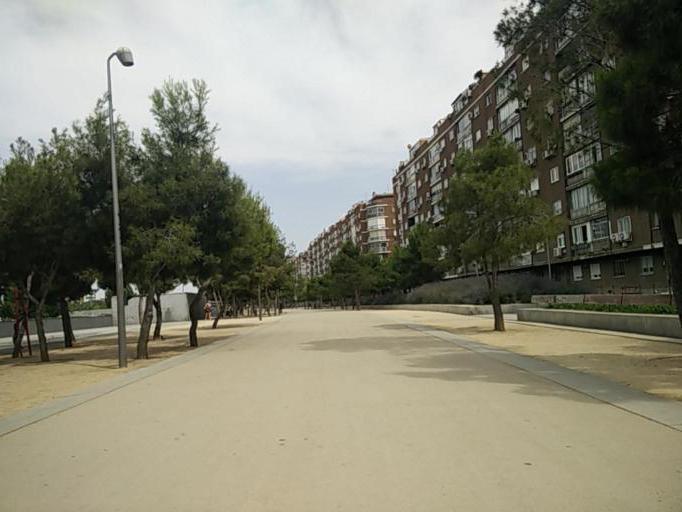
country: ES
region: Madrid
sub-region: Provincia de Madrid
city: Usera
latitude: 40.3965
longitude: -3.7103
